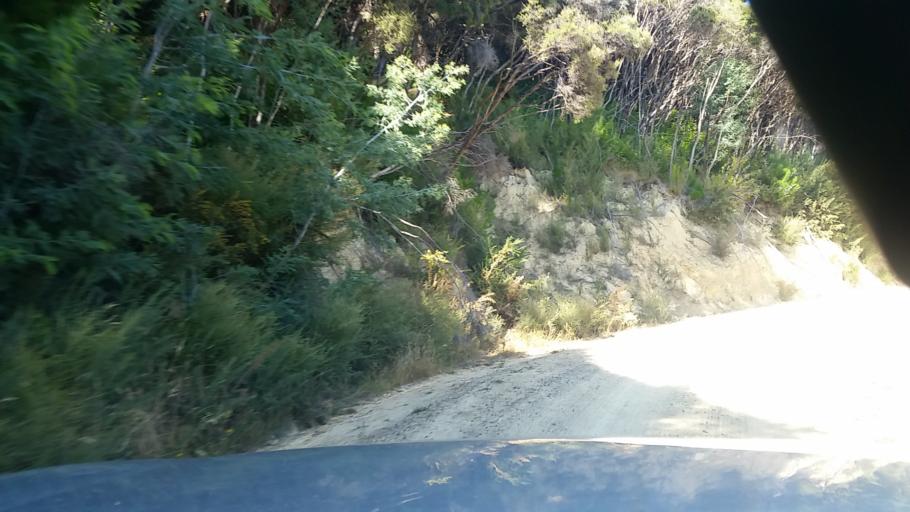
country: NZ
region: Marlborough
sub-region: Marlborough District
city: Picton
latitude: -41.3054
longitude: 174.1760
